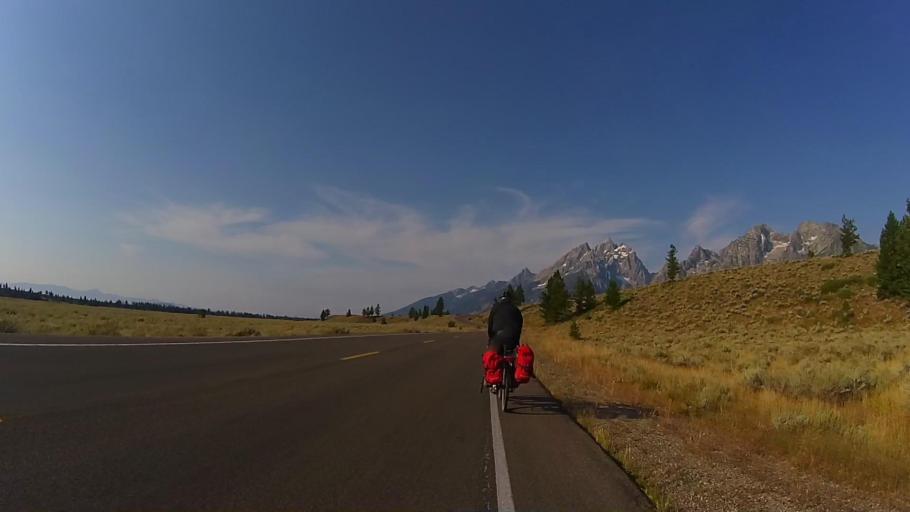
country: US
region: Wyoming
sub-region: Teton County
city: Moose Wilson Road
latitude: 43.7978
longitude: -110.6871
